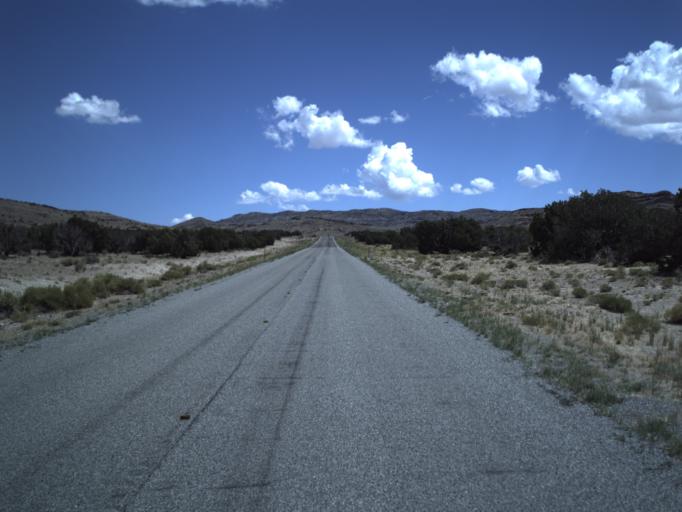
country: US
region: Utah
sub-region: Beaver County
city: Milford
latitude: 39.0741
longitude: -113.7174
